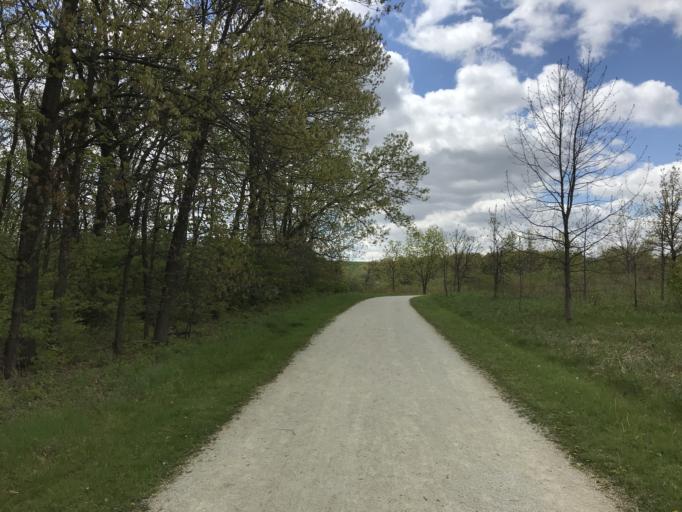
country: US
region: Illinois
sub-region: DuPage County
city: Woodridge
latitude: 41.7377
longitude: -88.0855
